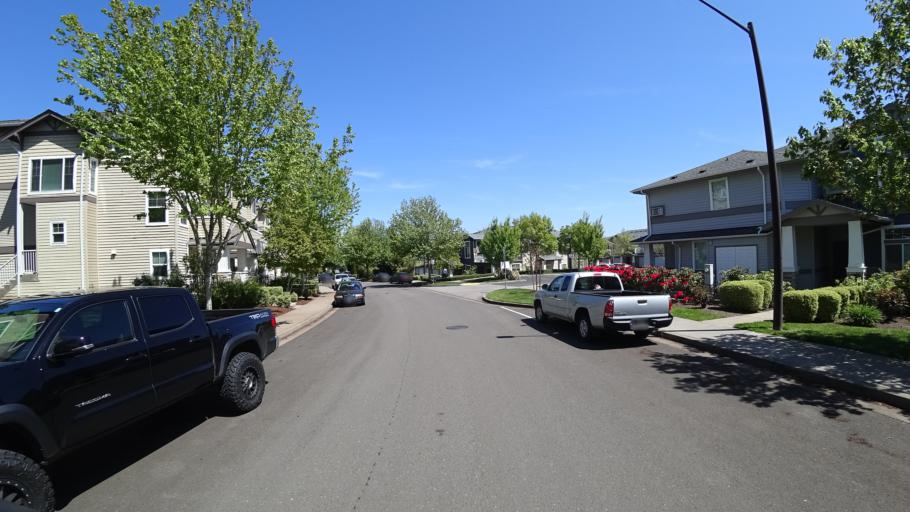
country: US
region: Oregon
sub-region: Washington County
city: King City
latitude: 45.4313
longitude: -122.8332
